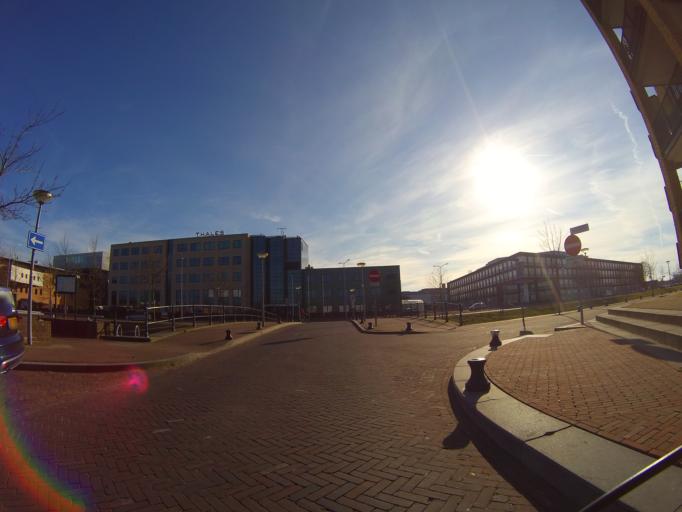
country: NL
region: North Holland
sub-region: Gemeente Huizen
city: Huizen
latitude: 52.3060
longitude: 5.2413
